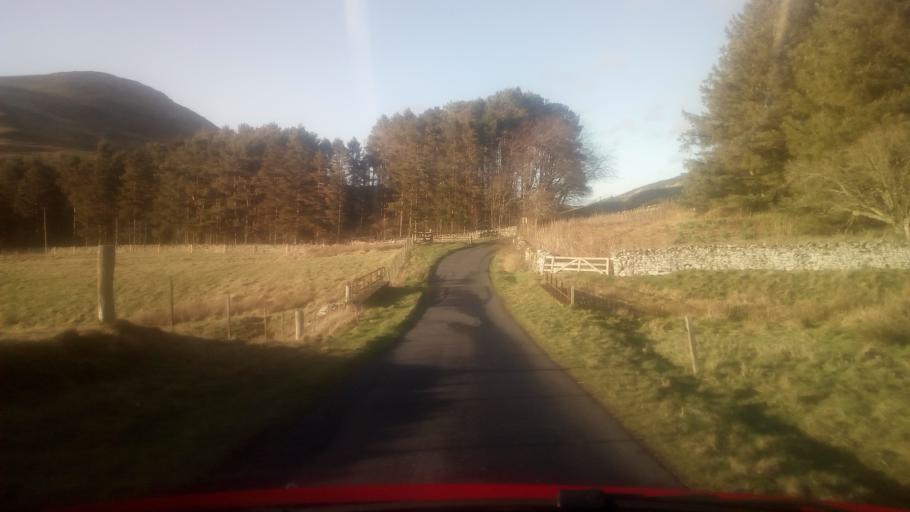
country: GB
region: Scotland
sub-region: The Scottish Borders
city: Kelso
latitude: 55.4376
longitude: -2.3635
